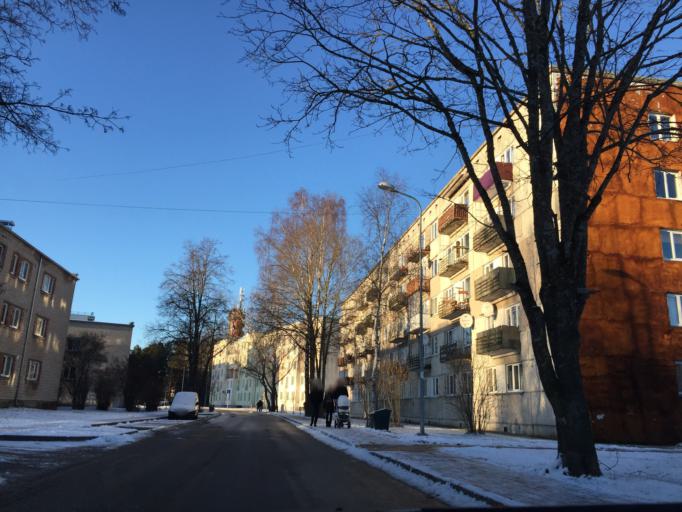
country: LV
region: Kekava
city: Balozi
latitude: 56.8778
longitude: 24.1218
